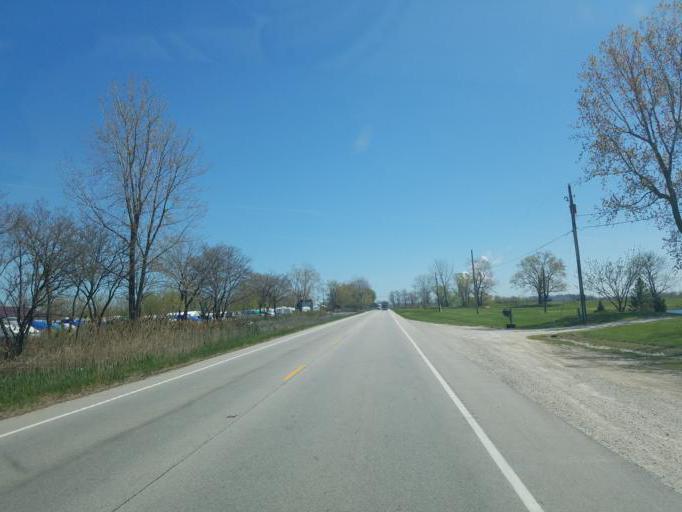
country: US
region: Ohio
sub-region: Ottawa County
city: Oak Harbor
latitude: 41.6038
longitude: -83.1383
